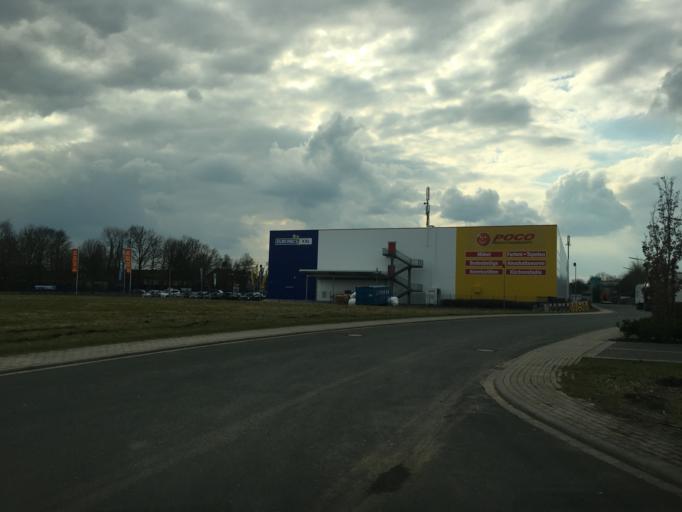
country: DE
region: North Rhine-Westphalia
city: Ludinghausen
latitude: 51.7735
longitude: 7.4669
